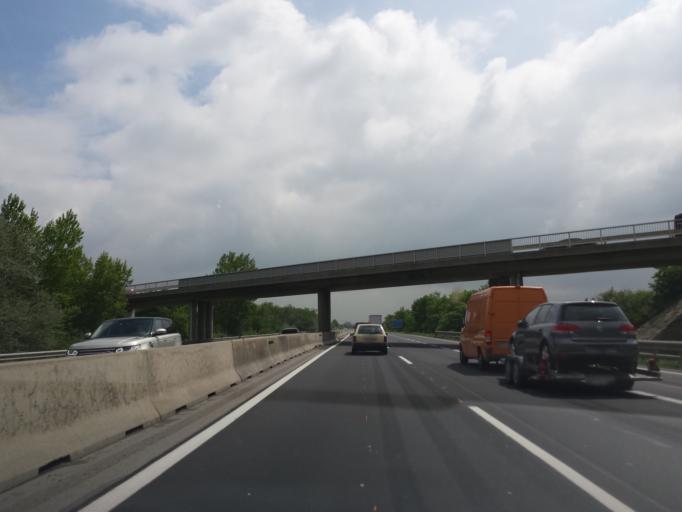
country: AT
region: Burgenland
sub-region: Politischer Bezirk Neusiedl am See
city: Bruckneudorf
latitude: 48.0361
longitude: 16.8128
